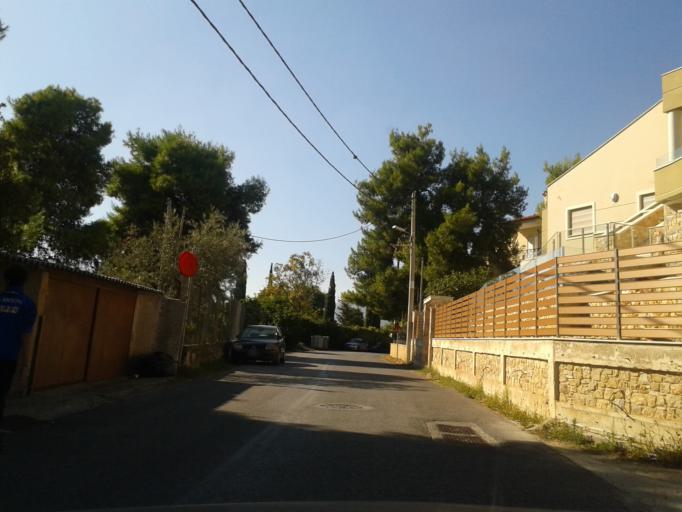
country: GR
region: Attica
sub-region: Nomarchia Anatolikis Attikis
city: Anoixi
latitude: 38.1297
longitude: 23.8647
